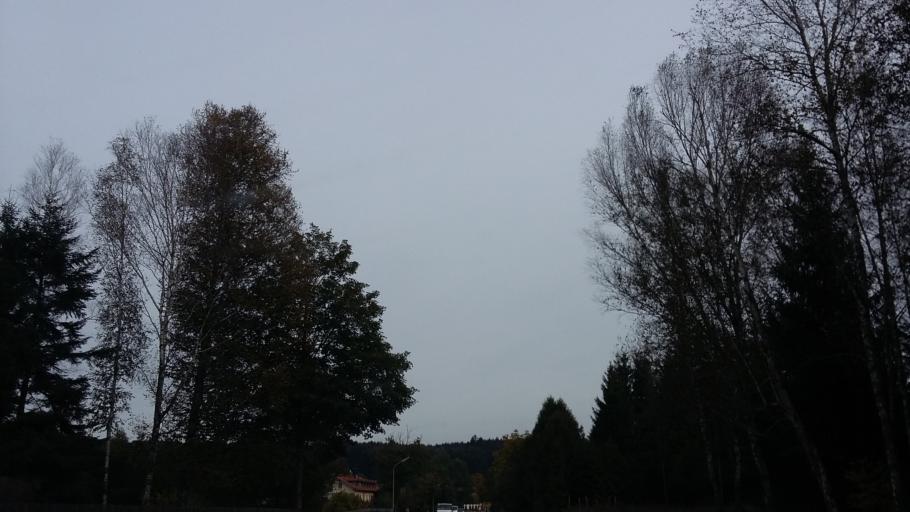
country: DE
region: Bavaria
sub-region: Upper Bavaria
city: Wolfratshausen
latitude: 47.9309
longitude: 11.3906
